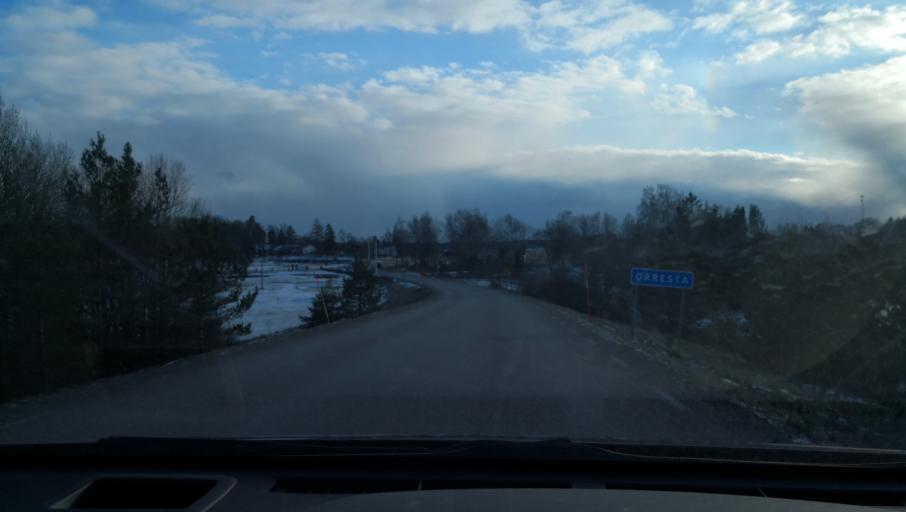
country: SE
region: Uppsala
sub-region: Enkopings Kommun
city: Irsta
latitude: 59.6652
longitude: 16.8372
